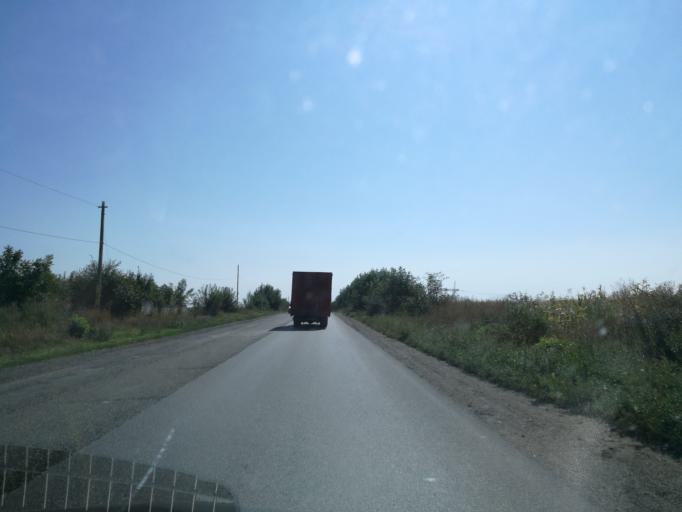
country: RO
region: Neamt
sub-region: Comuna Botesti
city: Barticesti
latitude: 47.0497
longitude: 26.7987
